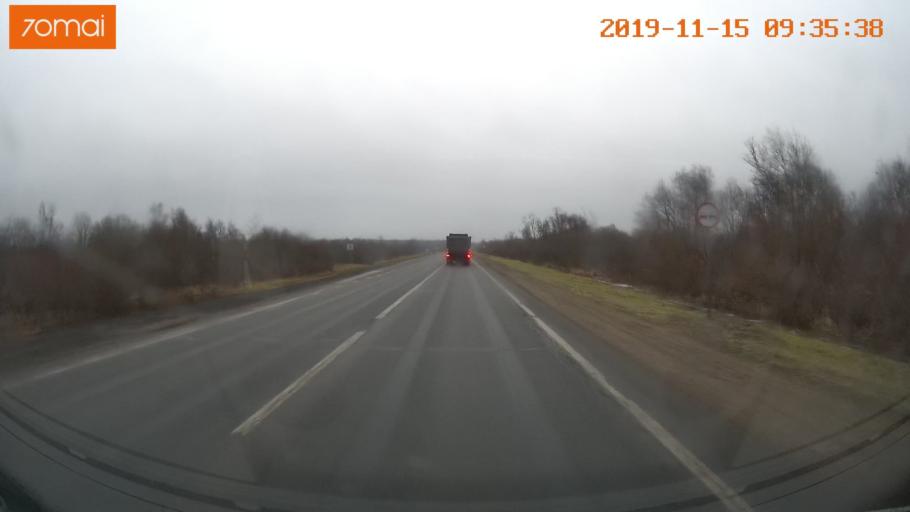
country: RU
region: Vologda
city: Sheksna
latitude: 59.2531
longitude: 38.4036
